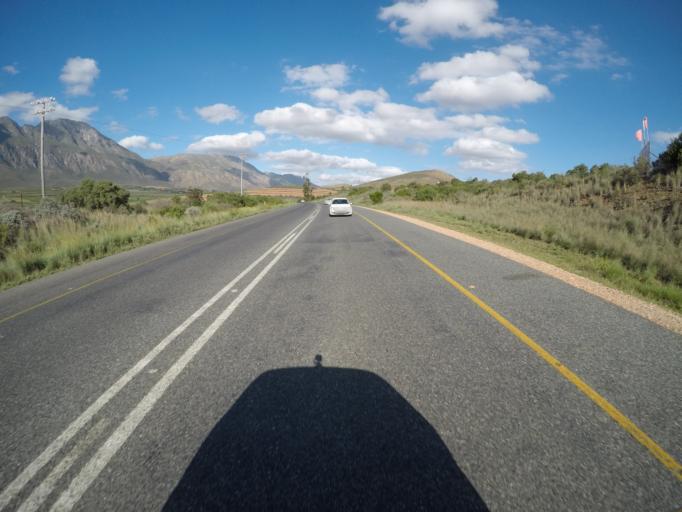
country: ZA
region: Western Cape
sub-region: Cape Winelands District Municipality
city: Ashton
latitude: -33.8651
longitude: 20.1192
